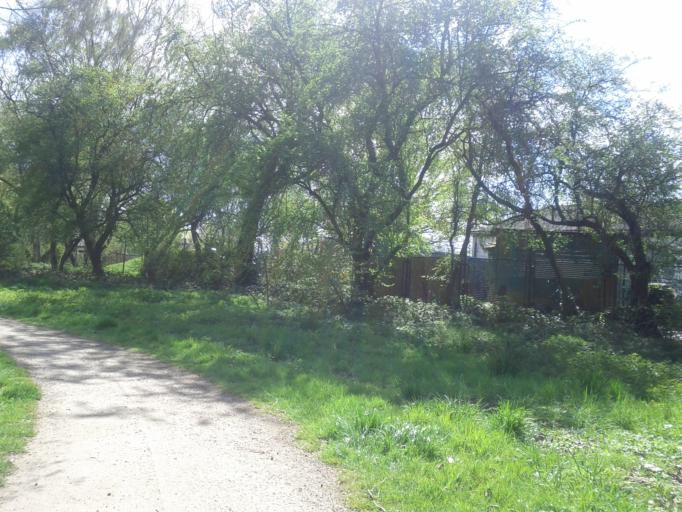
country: DE
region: North Rhine-Westphalia
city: Lanstrop
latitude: 51.5766
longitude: 7.5631
